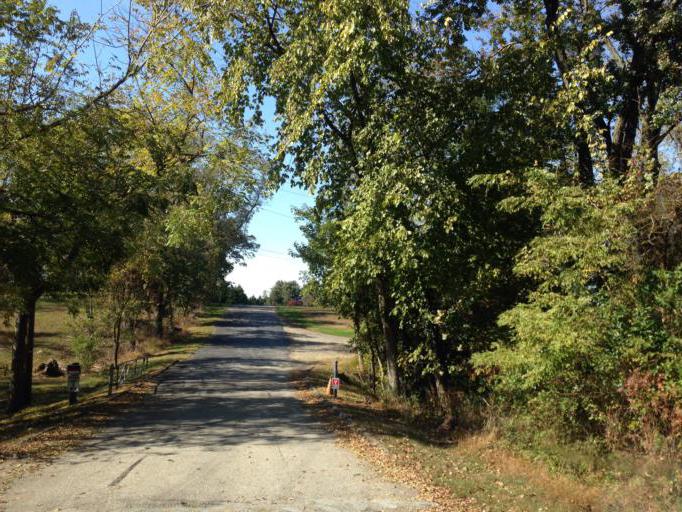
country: US
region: Maryland
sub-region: Howard County
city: Columbia
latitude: 39.2523
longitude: -76.8246
